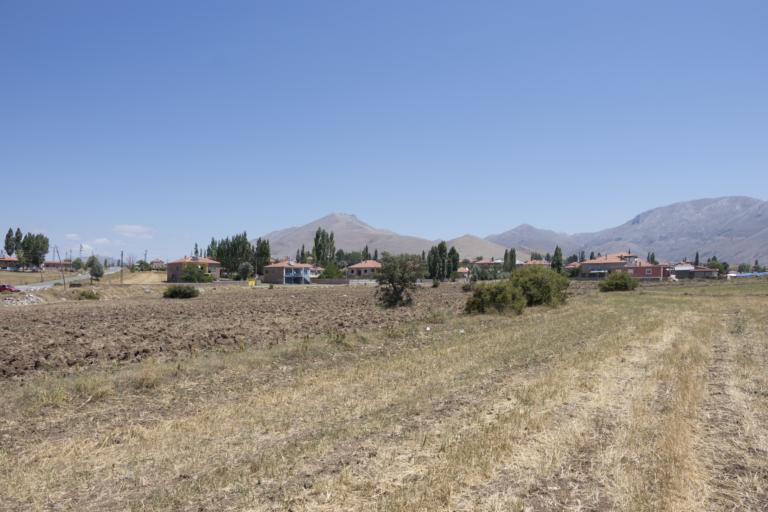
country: TR
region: Kayseri
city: Toklar
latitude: 38.4060
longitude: 36.0726
